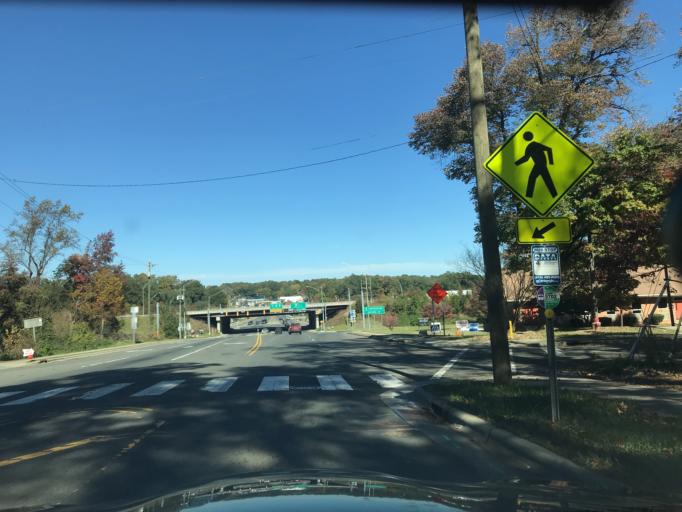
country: US
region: North Carolina
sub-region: Durham County
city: Durham
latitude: 36.0126
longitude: -78.8910
